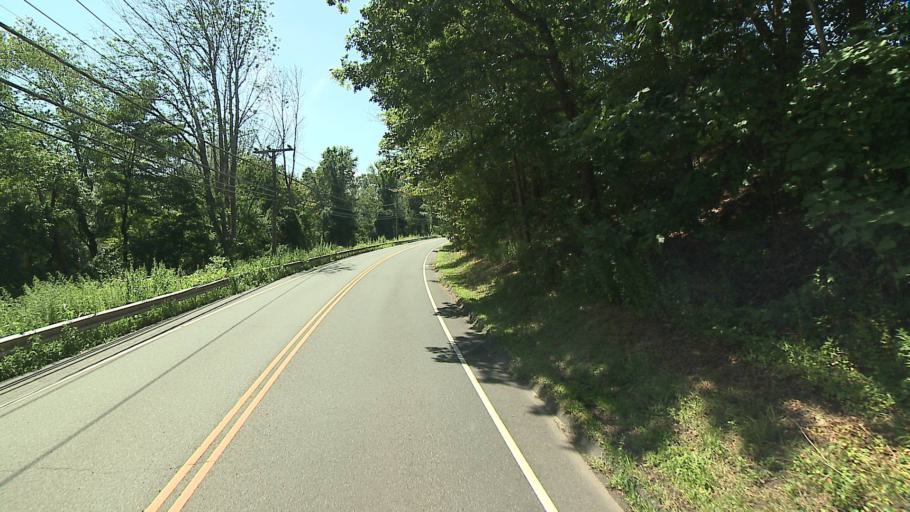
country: US
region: Connecticut
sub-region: New Haven County
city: Oxford
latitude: 41.3590
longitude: -73.1932
